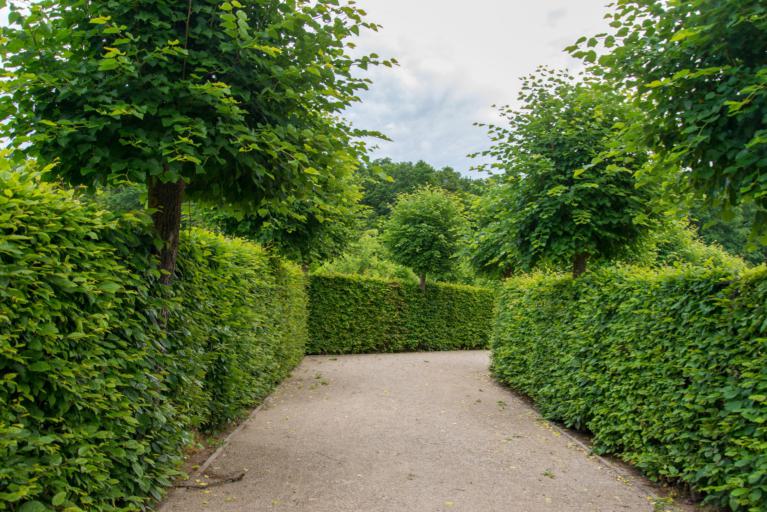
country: DE
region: Bavaria
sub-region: Upper Franconia
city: Neunkirchen am Main
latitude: 49.9463
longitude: 11.6208
